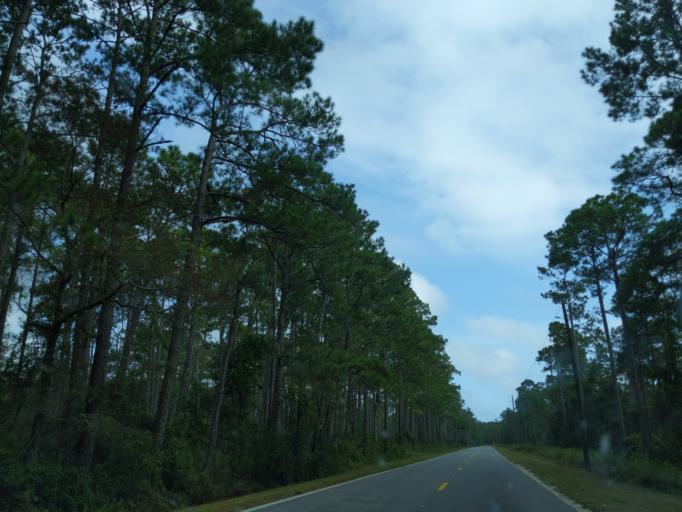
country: US
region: Florida
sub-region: Wakulla County
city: Crawfordville
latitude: 30.1143
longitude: -84.3112
